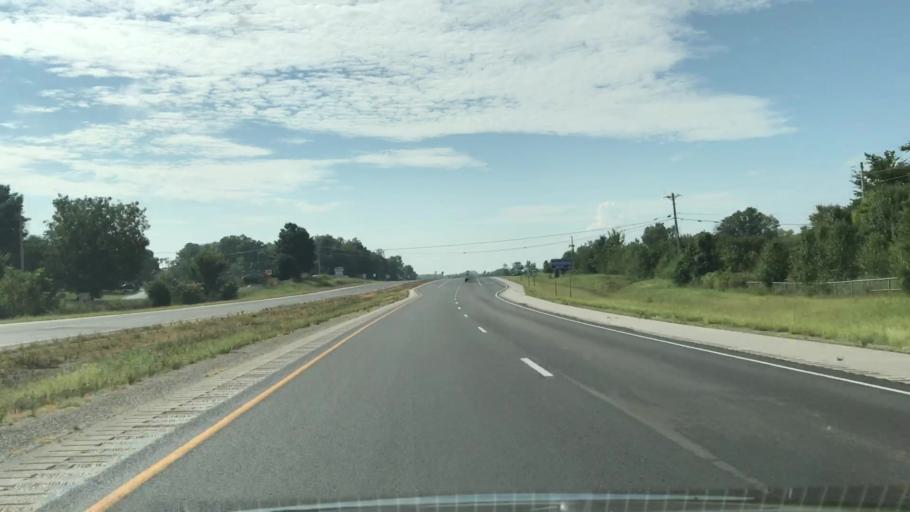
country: US
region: Kentucky
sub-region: Warren County
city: Plano
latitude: 36.8758
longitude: -86.3554
